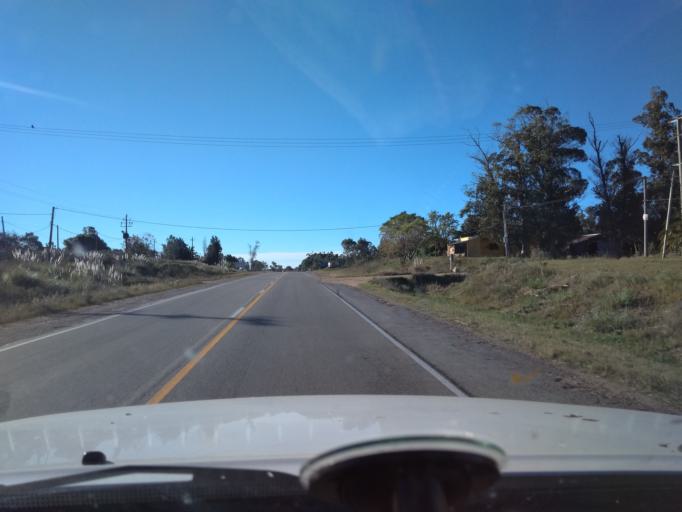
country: UY
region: Canelones
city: Sauce
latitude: -34.6124
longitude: -56.0488
